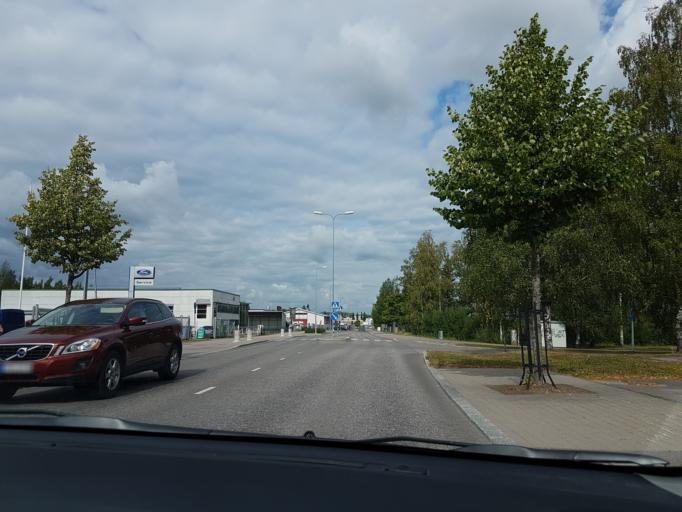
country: FI
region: Uusimaa
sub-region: Helsinki
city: Jaervenpaeae
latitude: 60.4721
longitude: 25.1164
